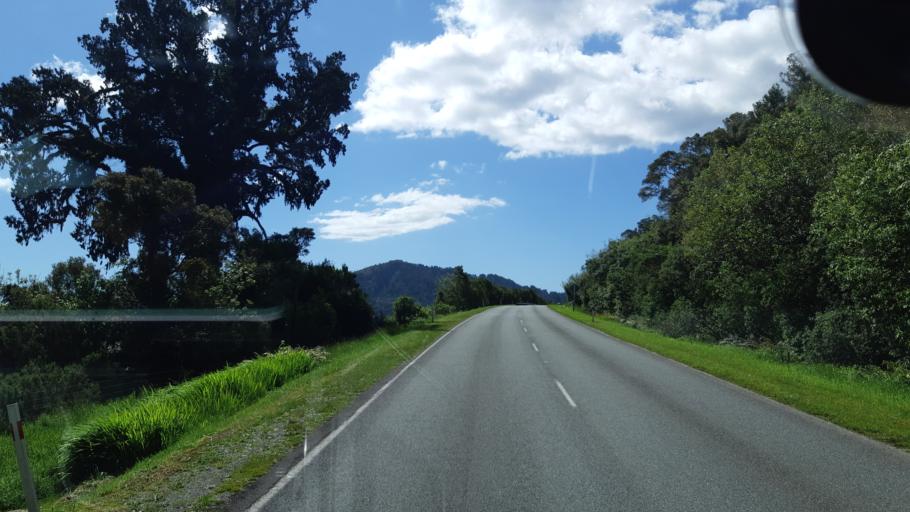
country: NZ
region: West Coast
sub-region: Westland District
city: Hokitika
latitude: -43.0897
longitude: 170.6265
